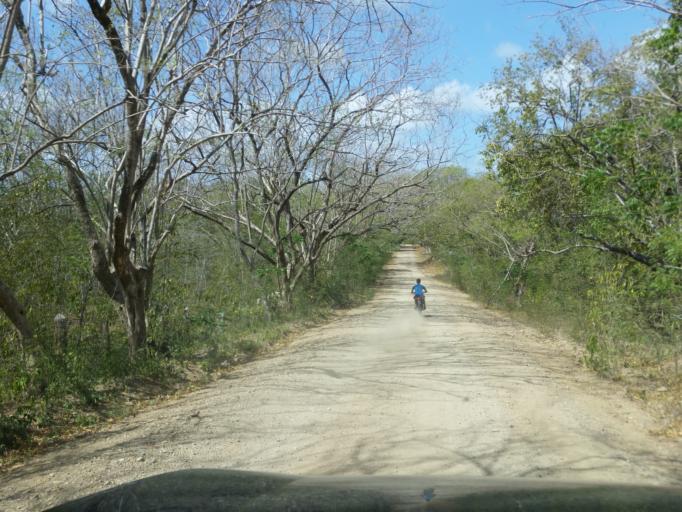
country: CR
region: Guanacaste
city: La Cruz
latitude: 11.1096
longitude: -85.7518
